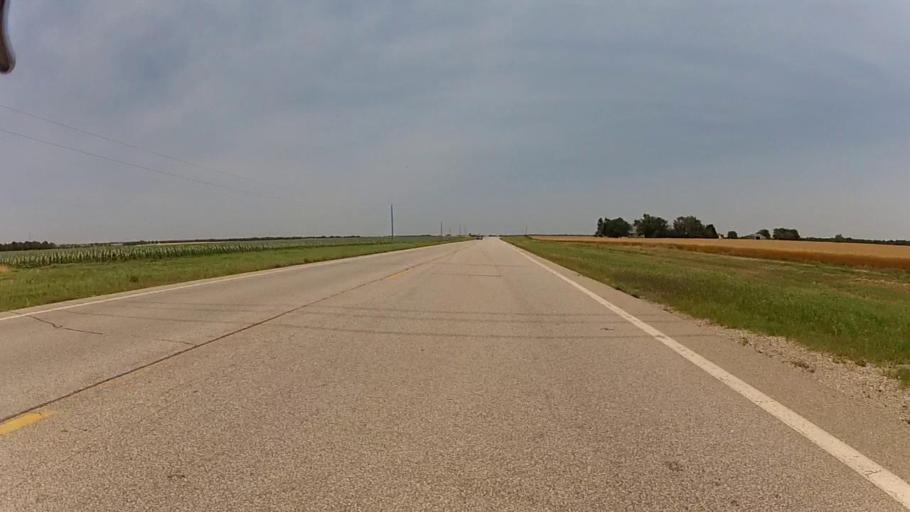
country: US
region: Kansas
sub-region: Cowley County
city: Arkansas City
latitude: 37.0563
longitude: -97.1349
